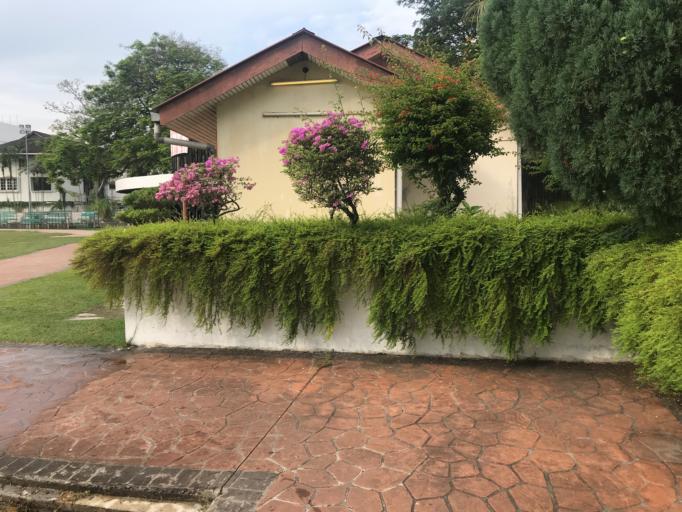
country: MY
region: Perak
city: Ipoh
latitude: 4.5989
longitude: 101.0757
